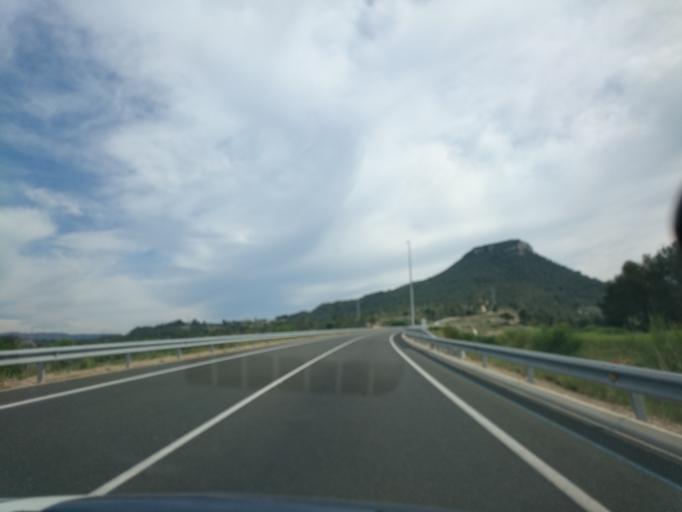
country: ES
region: Catalonia
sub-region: Provincia de Barcelona
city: Odena
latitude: 41.5952
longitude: 1.6625
